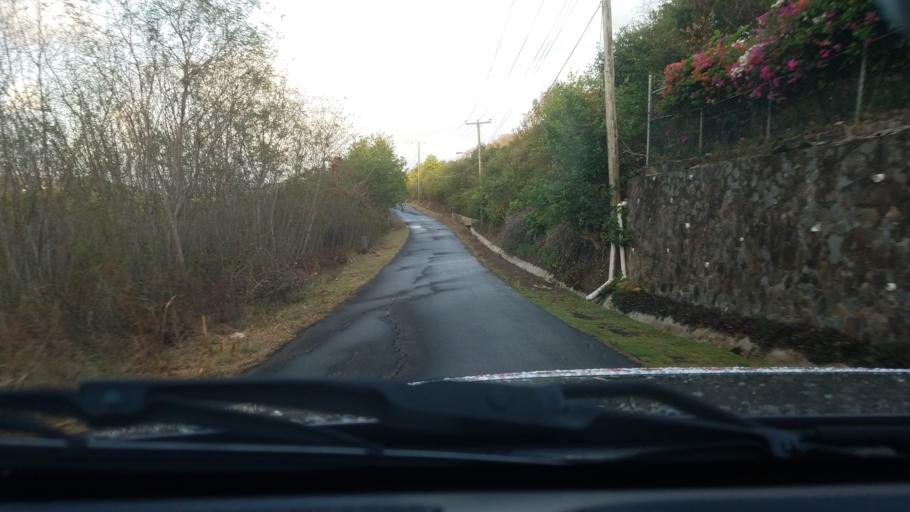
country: LC
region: Gros-Islet
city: Gros Islet
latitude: 14.0908
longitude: -60.9389
